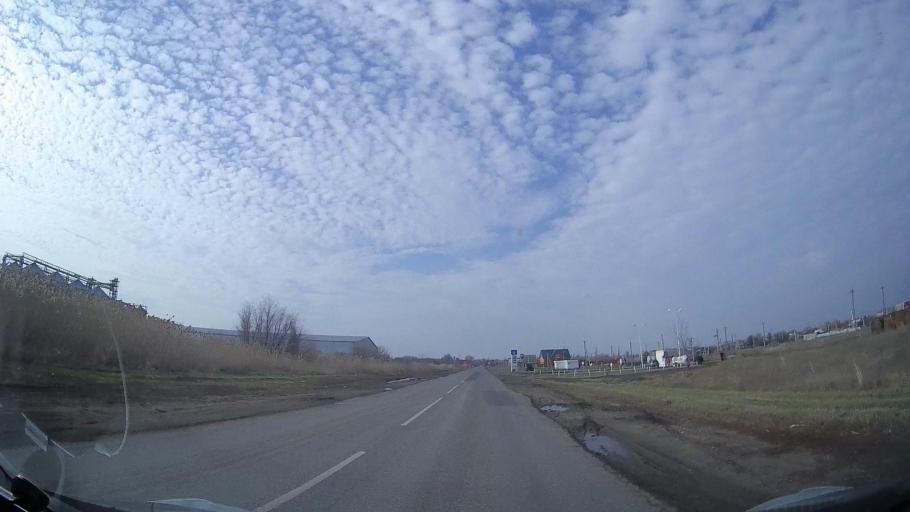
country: RU
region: Rostov
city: Veselyy
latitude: 47.0825
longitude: 40.7711
